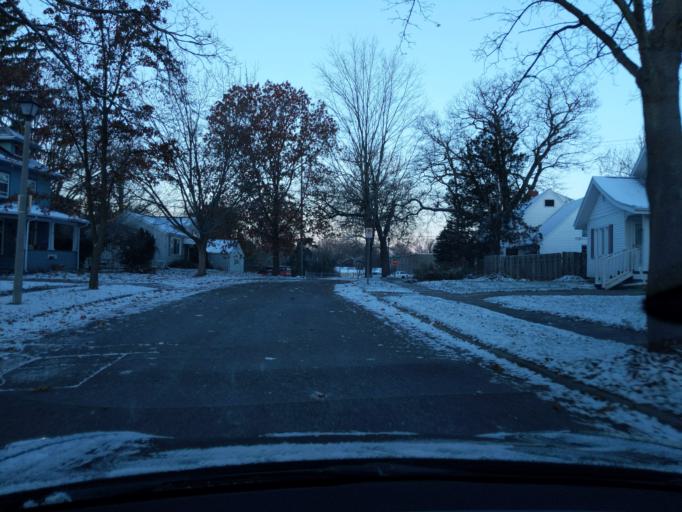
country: US
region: Michigan
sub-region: Ingham County
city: Lansing
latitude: 42.7061
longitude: -84.5561
